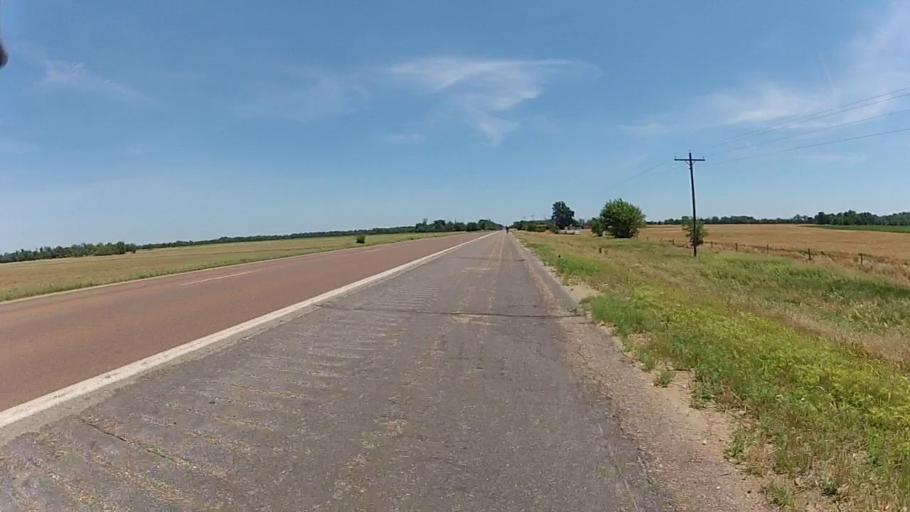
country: US
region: Kansas
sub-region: Barber County
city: Medicine Lodge
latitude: 37.2536
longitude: -98.3446
